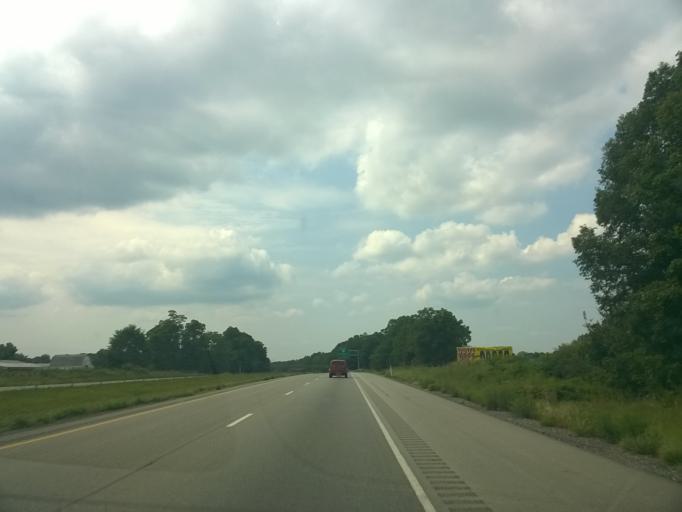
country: US
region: Indiana
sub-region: Putnam County
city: Cloverdale
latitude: 39.5333
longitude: -86.8485
